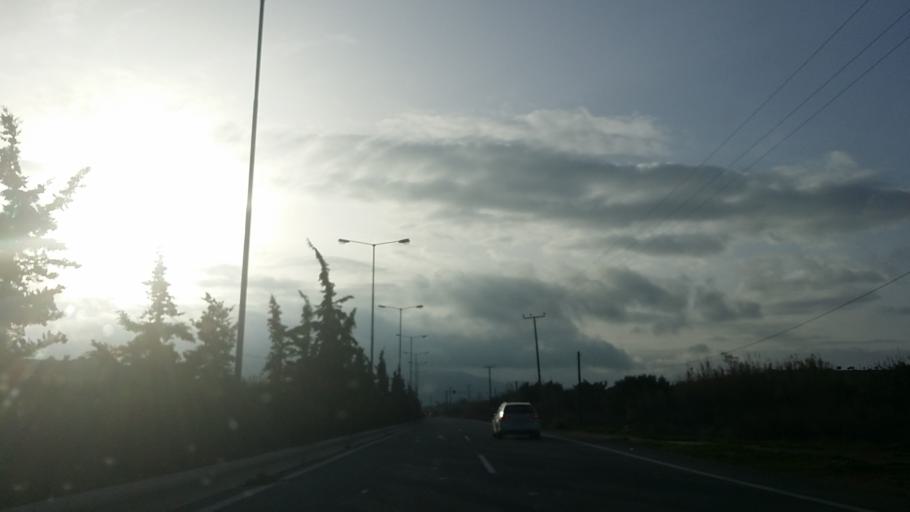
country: GR
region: Attica
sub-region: Nomarchia Anatolikis Attikis
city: Keratea
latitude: 37.8033
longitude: 24.0398
